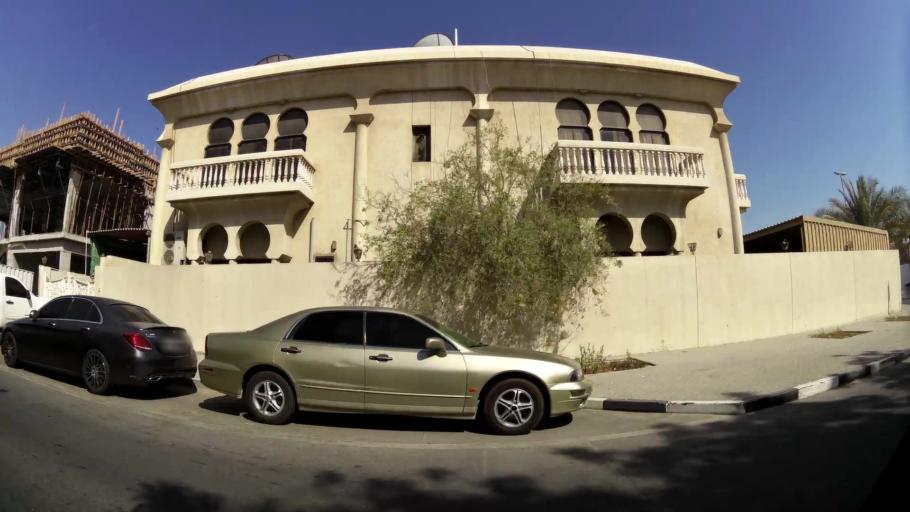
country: AE
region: Ash Shariqah
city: Sharjah
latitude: 25.2447
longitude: 55.2970
